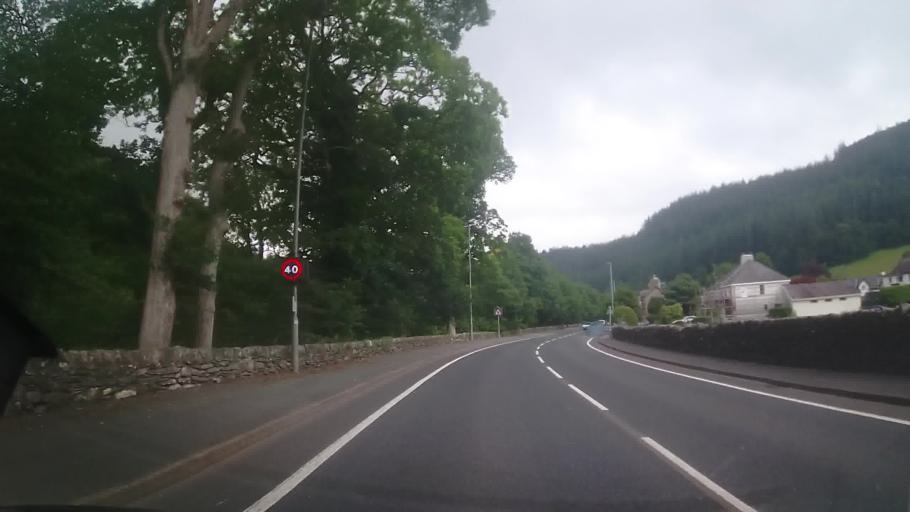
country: GB
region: Wales
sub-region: Conwy
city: Betws-y-Coed
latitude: 53.0936
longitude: -3.8207
